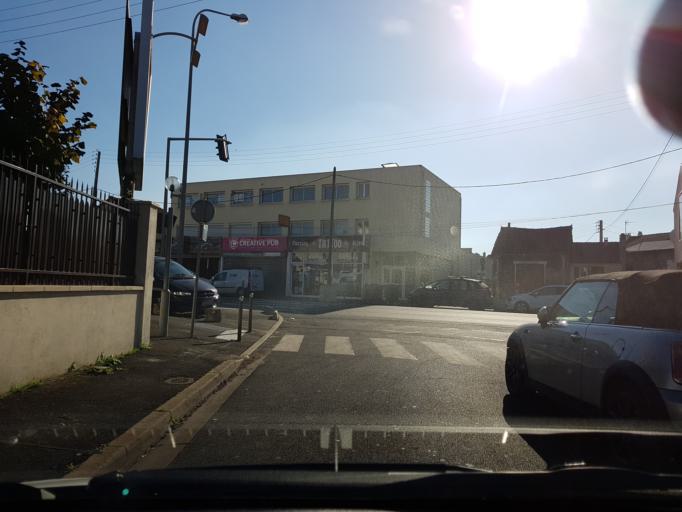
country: FR
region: Ile-de-France
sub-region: Departement du Val-de-Marne
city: Chennevieres-sur-Marne
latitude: 48.8017
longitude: 2.5408
